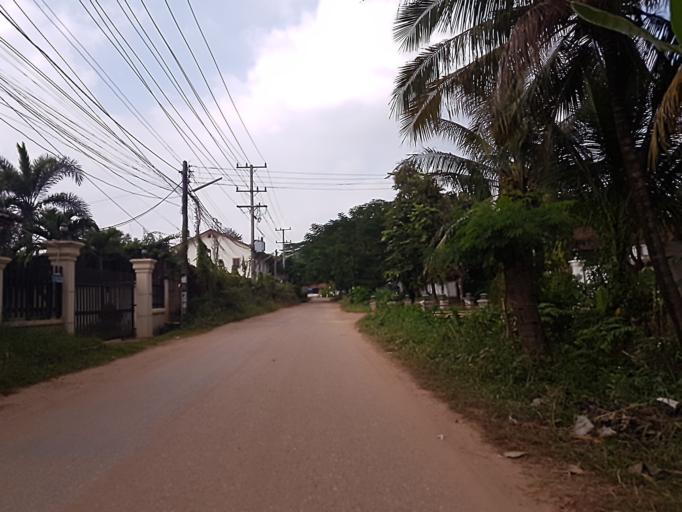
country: LA
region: Vientiane
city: Vientiane
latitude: 17.9291
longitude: 102.6259
